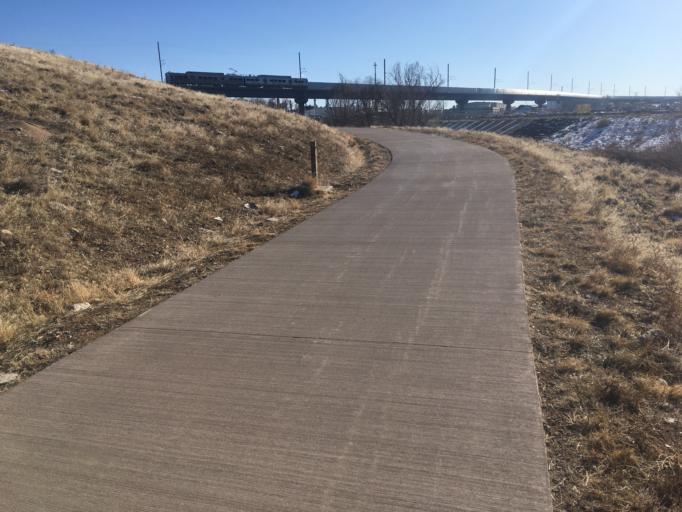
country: US
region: Colorado
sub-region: Adams County
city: Commerce City
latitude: 39.8116
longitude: -104.9517
